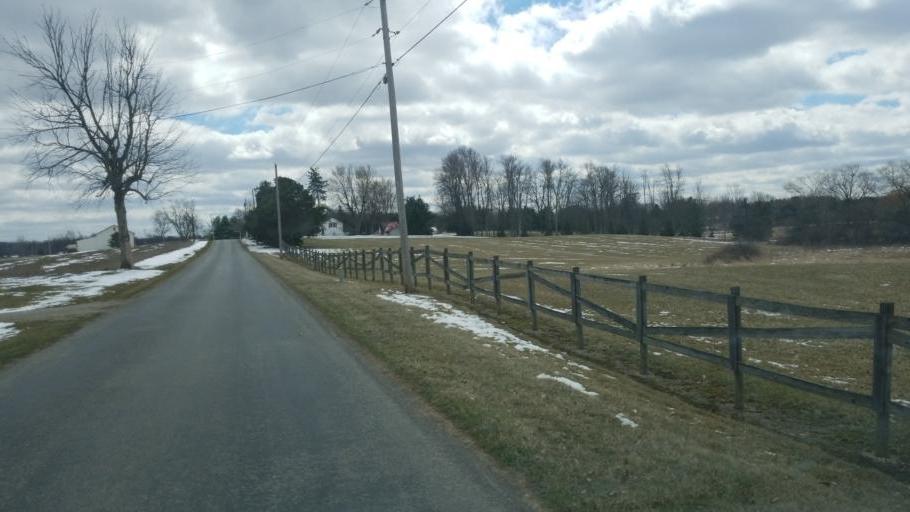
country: US
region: Ohio
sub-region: Richland County
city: Shelby
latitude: 40.8473
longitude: -82.5980
